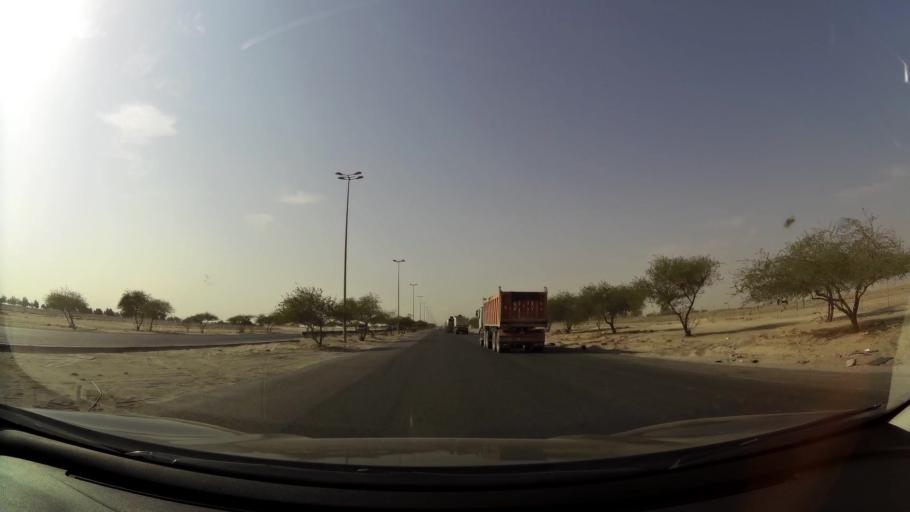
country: KW
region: Al Ahmadi
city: Al Ahmadi
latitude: 28.9415
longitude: 48.1127
